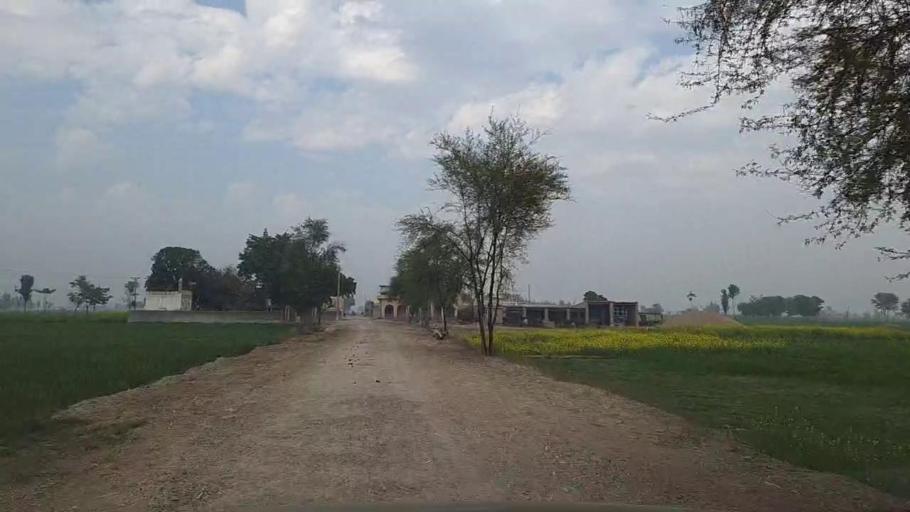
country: PK
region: Sindh
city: Nawabshah
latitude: 26.3563
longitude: 68.3921
